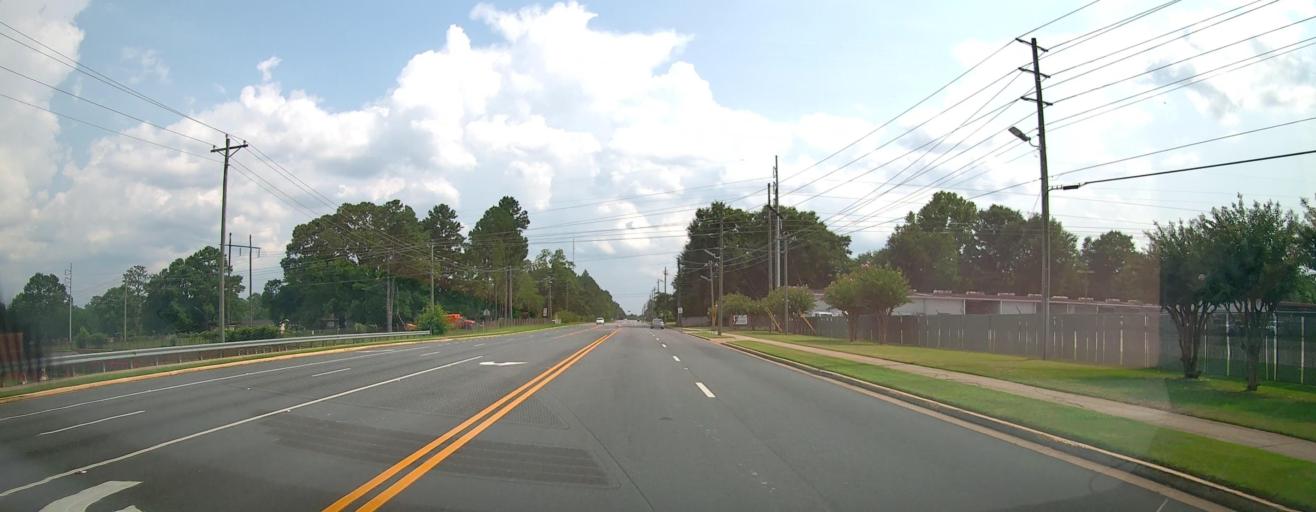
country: US
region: Georgia
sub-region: Houston County
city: Warner Robins
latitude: 32.6090
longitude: -83.6131
